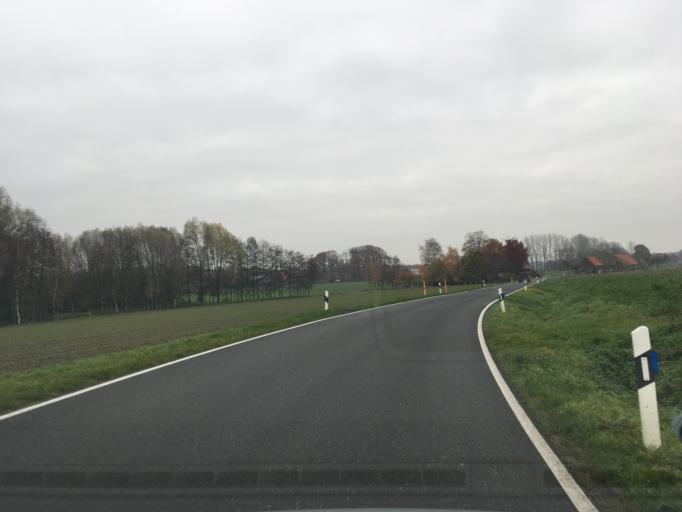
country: DE
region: North Rhine-Westphalia
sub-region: Regierungsbezirk Munster
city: Legden
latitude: 52.0333
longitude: 7.1199
